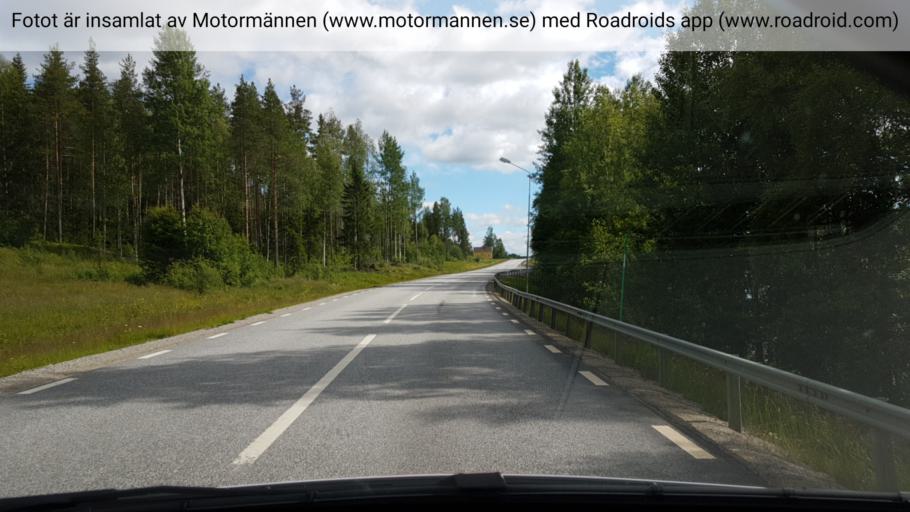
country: SE
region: Vaesterbotten
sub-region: Vindelns Kommun
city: Vindeln
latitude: 64.1494
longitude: 19.5138
